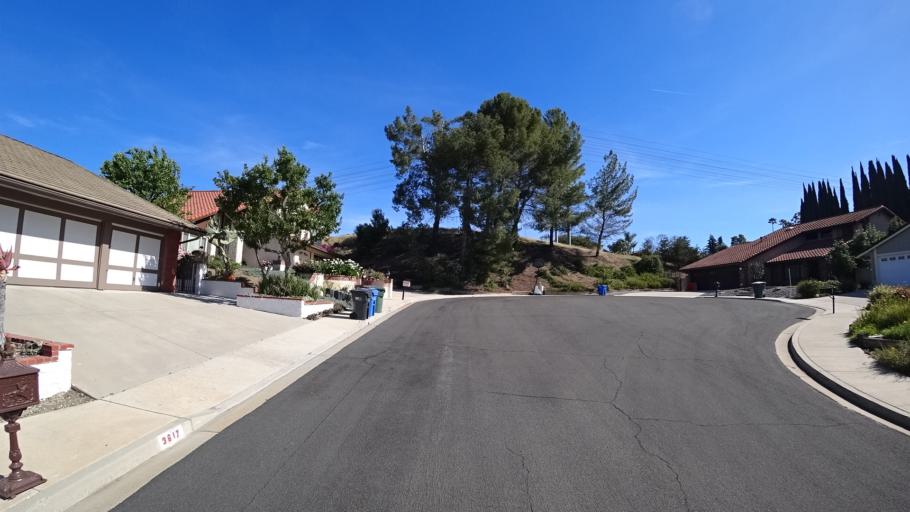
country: US
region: California
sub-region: Ventura County
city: Thousand Oaks
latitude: 34.2290
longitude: -118.8565
